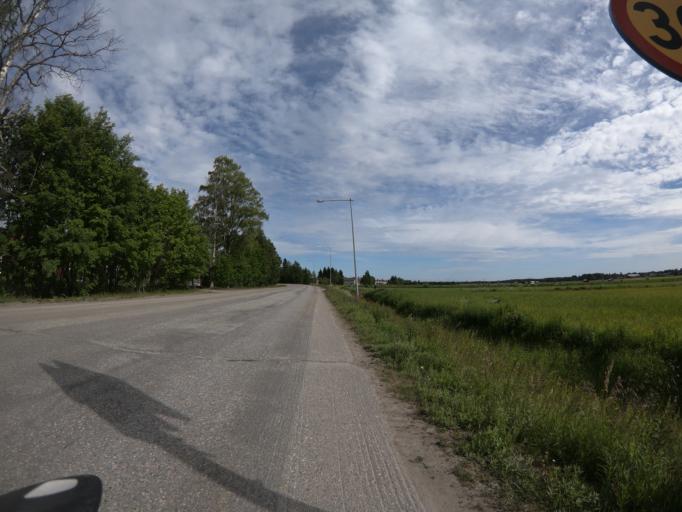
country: SE
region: Vaesterbotten
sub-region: Umea Kommun
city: Umea
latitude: 63.8221
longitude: 20.2418
